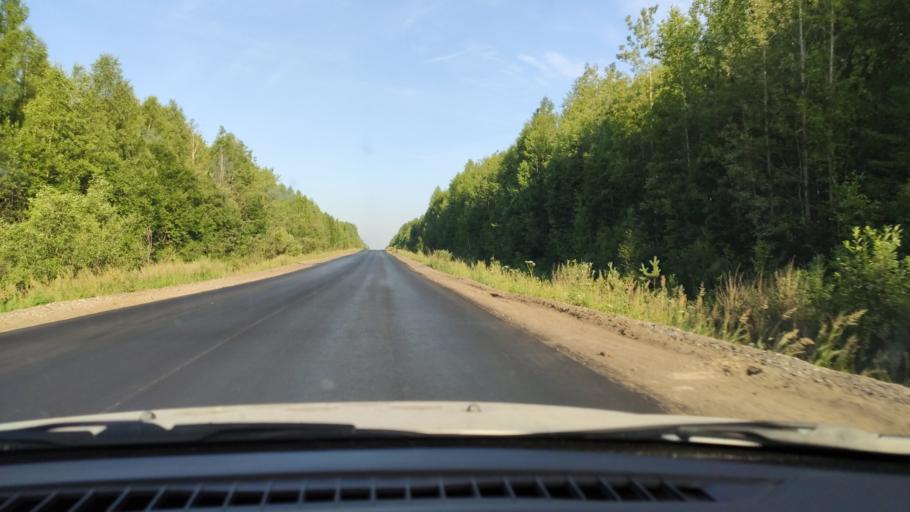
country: RU
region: Kirov
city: Chernaya Kholunitsa
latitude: 58.8804
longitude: 51.4415
